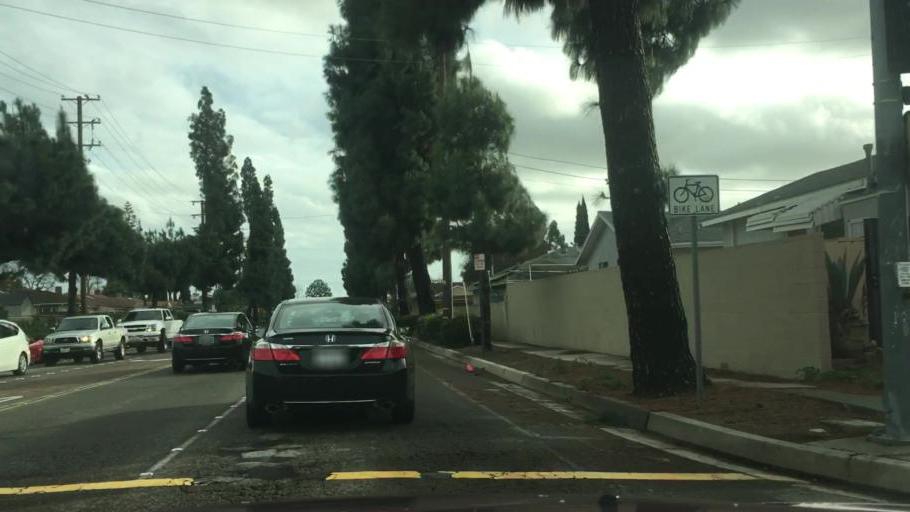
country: US
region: California
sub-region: Los Angeles County
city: East La Mirada
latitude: 33.9360
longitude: -117.9932
